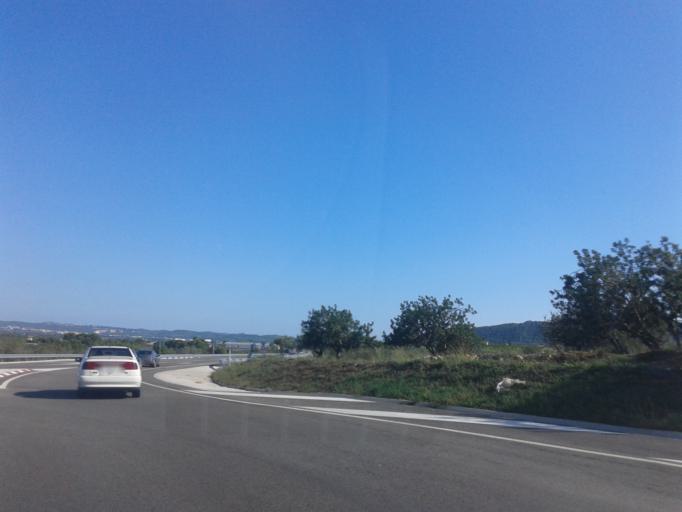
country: ES
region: Catalonia
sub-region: Provincia de Tarragona
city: Albinyana
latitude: 41.2604
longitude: 1.4965
